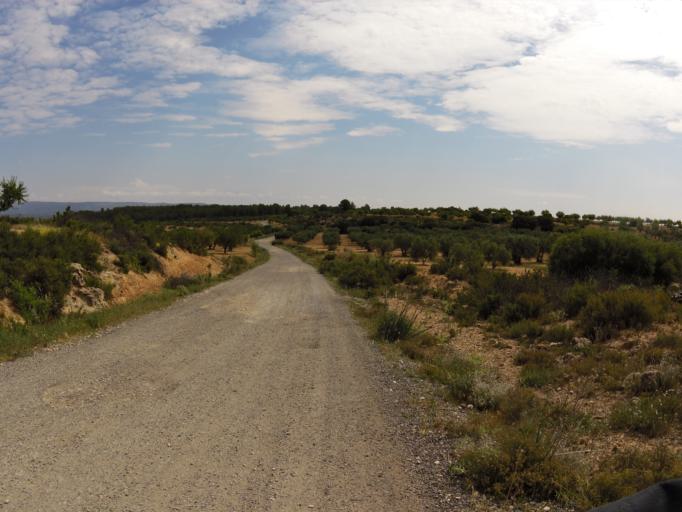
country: ES
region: Castille-La Mancha
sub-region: Provincia de Albacete
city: Casas Ibanez
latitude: 39.3526
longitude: -1.4797
